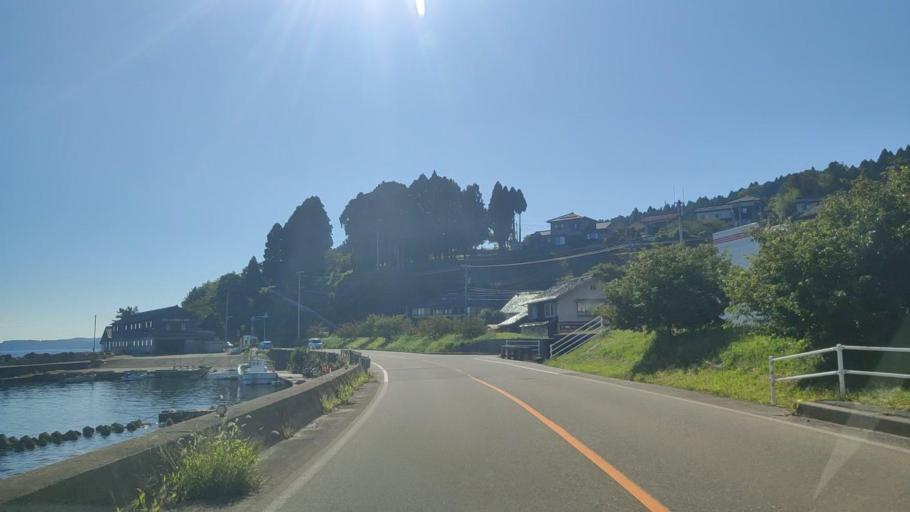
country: JP
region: Ishikawa
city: Nanao
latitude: 37.2888
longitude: 137.1169
